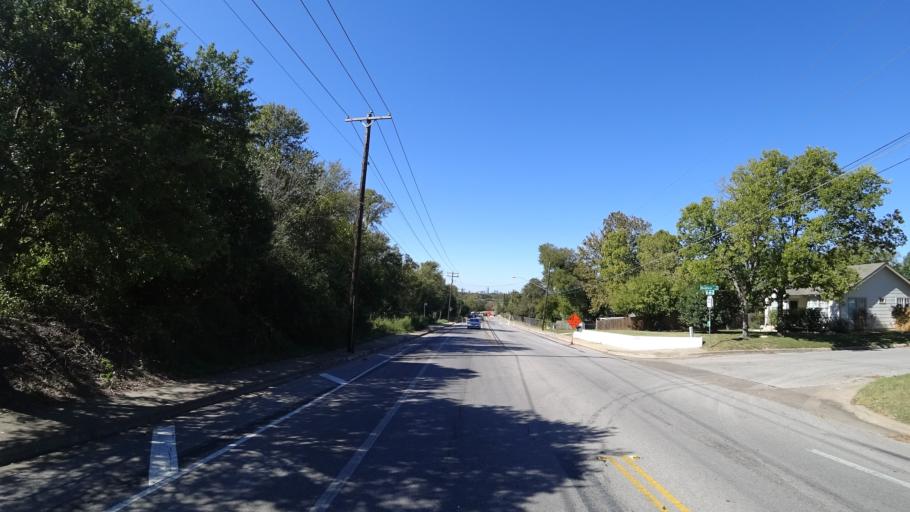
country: US
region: Texas
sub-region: Travis County
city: Austin
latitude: 30.2832
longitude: -97.6741
